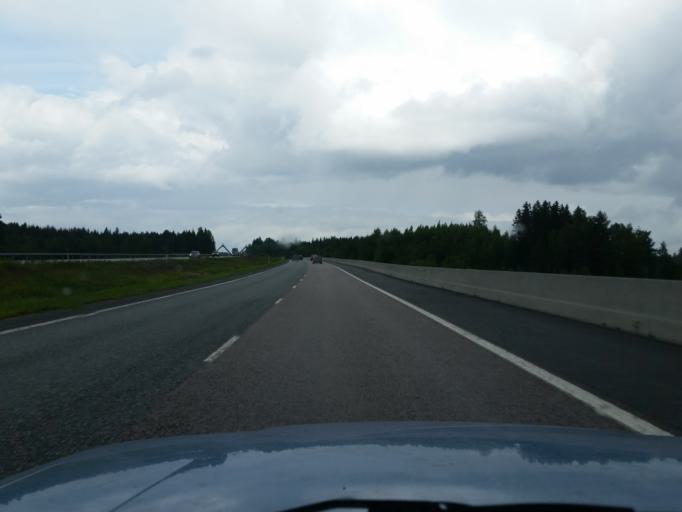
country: FI
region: Paijanne Tavastia
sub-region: Lahti
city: Nastola
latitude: 61.0792
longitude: 25.8910
